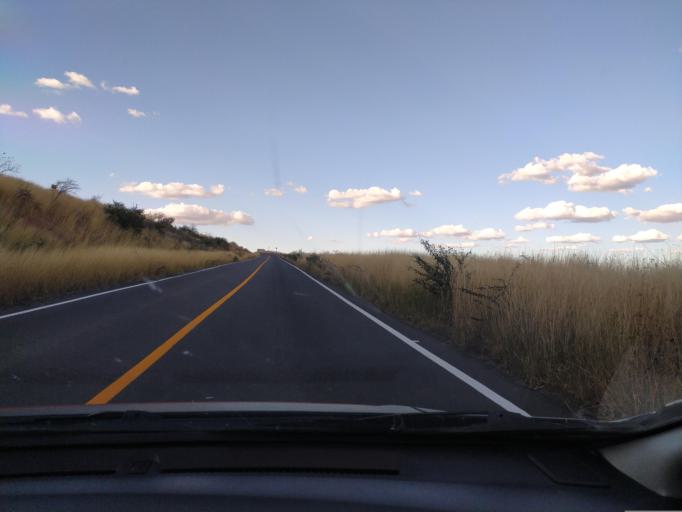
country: MX
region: Guanajuato
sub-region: Purisima del Rincon
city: Monte Grande
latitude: 21.0192
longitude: -101.8961
